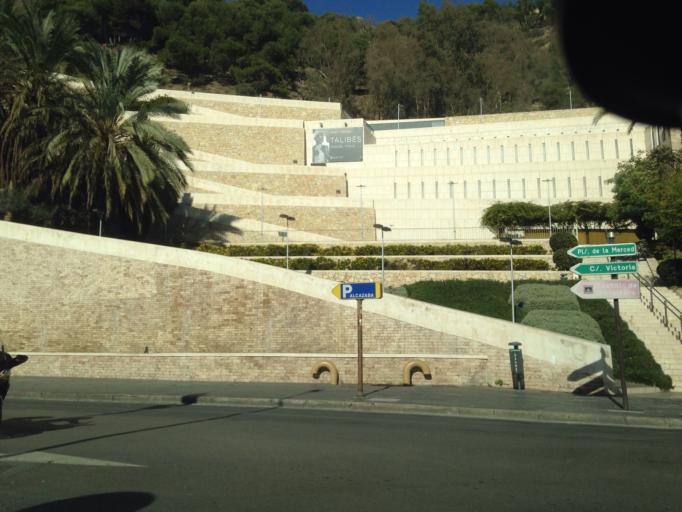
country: ES
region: Andalusia
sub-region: Provincia de Malaga
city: Malaga
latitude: 36.7211
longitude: -4.4129
